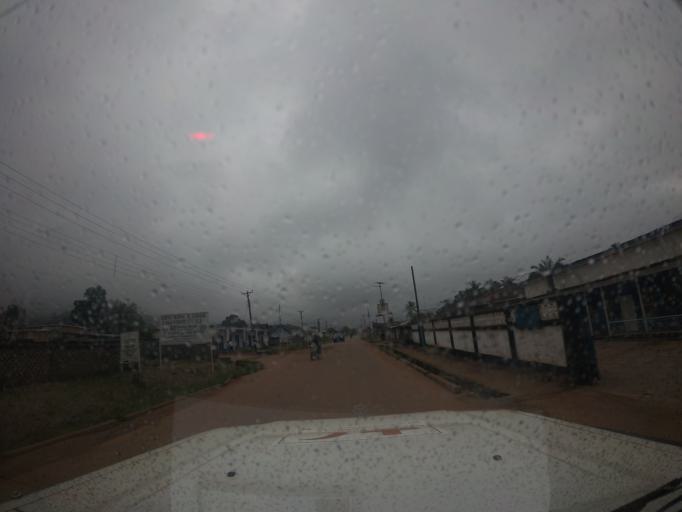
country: SL
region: Eastern Province
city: Kenema
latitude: 7.8883
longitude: -11.1877
